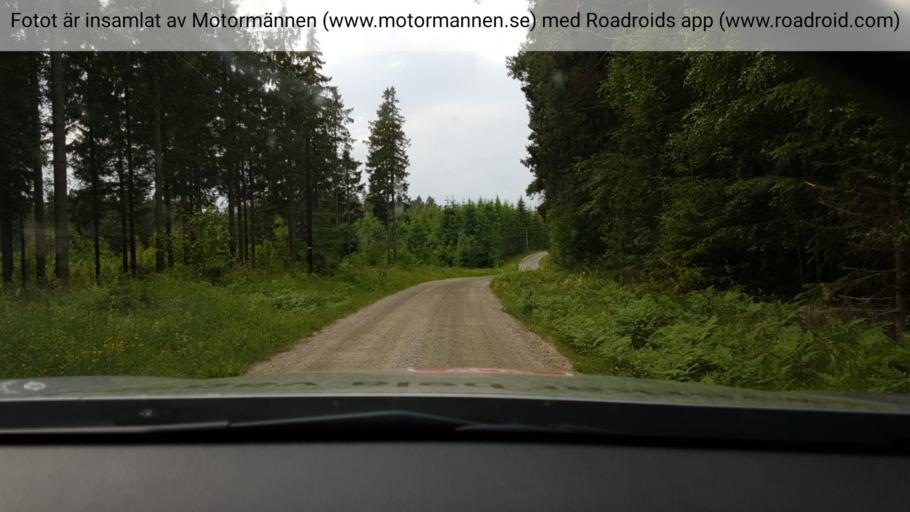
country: SE
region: Joenkoeping
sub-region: Mullsjo Kommun
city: Mullsjoe
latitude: 57.9191
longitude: 13.7212
